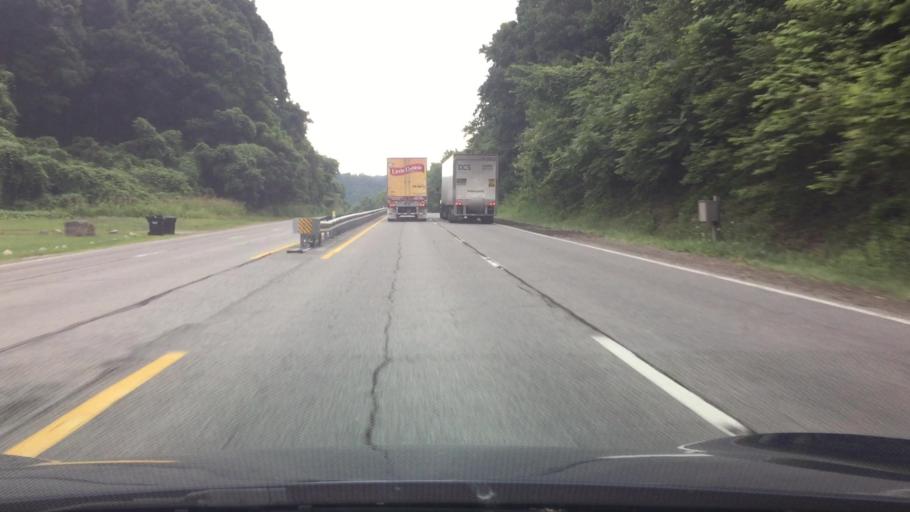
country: US
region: Virginia
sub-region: Montgomery County
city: Shawsville
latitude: 37.2399
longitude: -80.1824
